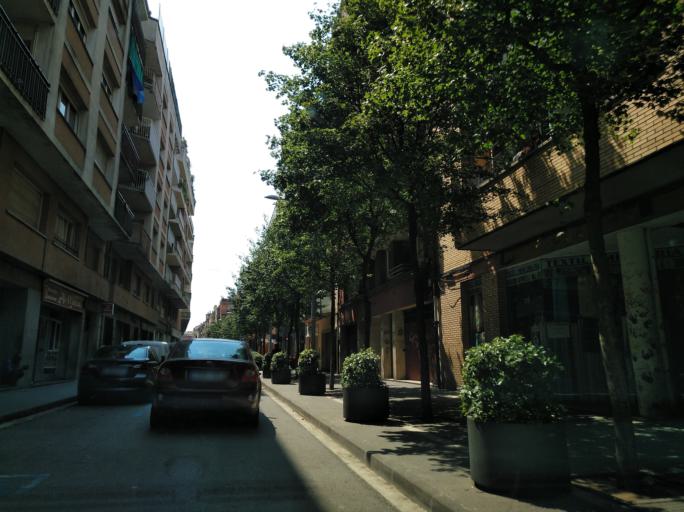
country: ES
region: Catalonia
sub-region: Provincia de Girona
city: Salt
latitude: 41.9740
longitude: 2.7899
